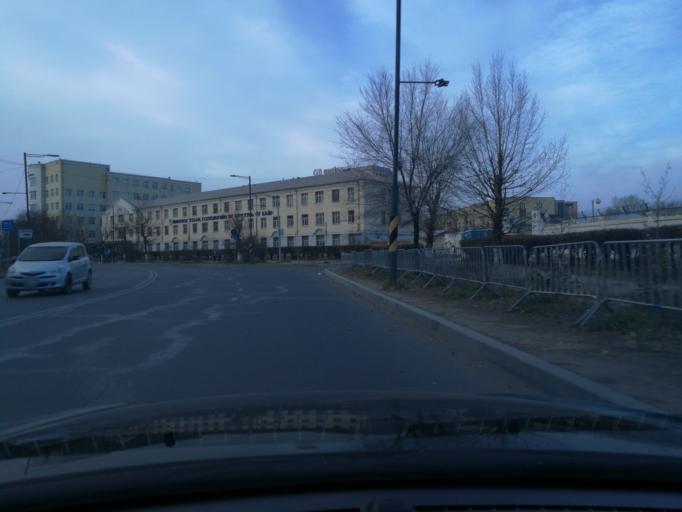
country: MN
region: Ulaanbaatar
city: Ulaanbaatar
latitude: 47.9240
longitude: 106.9227
